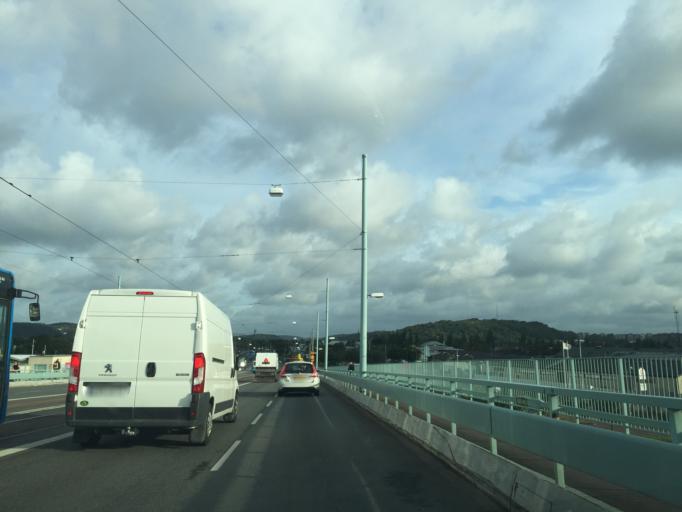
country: SE
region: Vaestra Goetaland
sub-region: Goteborg
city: Goeteborg
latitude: 57.7165
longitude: 11.9646
